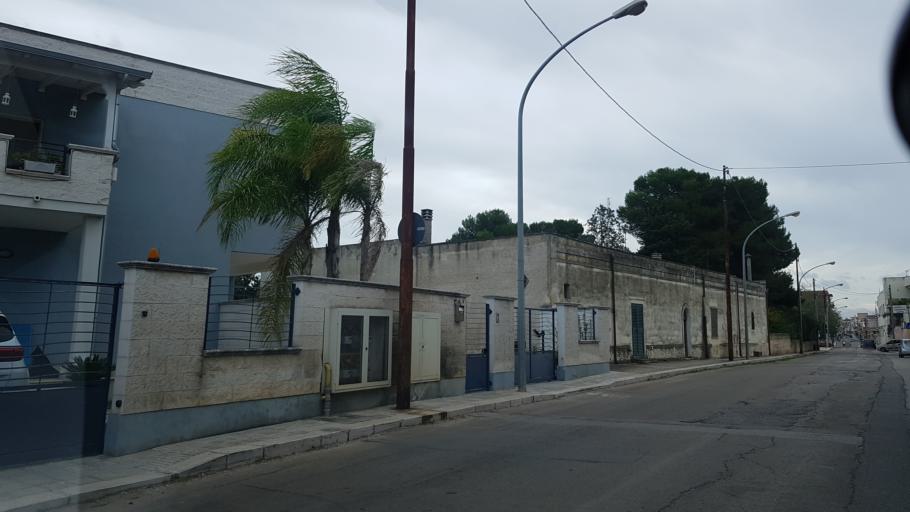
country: IT
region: Apulia
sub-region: Provincia di Brindisi
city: Mesagne
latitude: 40.5656
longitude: 17.8024
